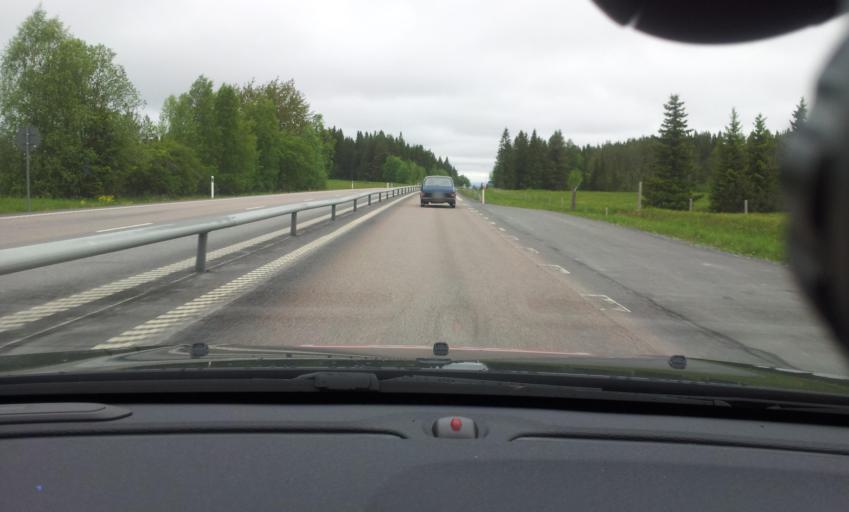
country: SE
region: Jaemtland
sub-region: Krokoms Kommun
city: Krokom
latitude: 63.2612
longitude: 14.5485
